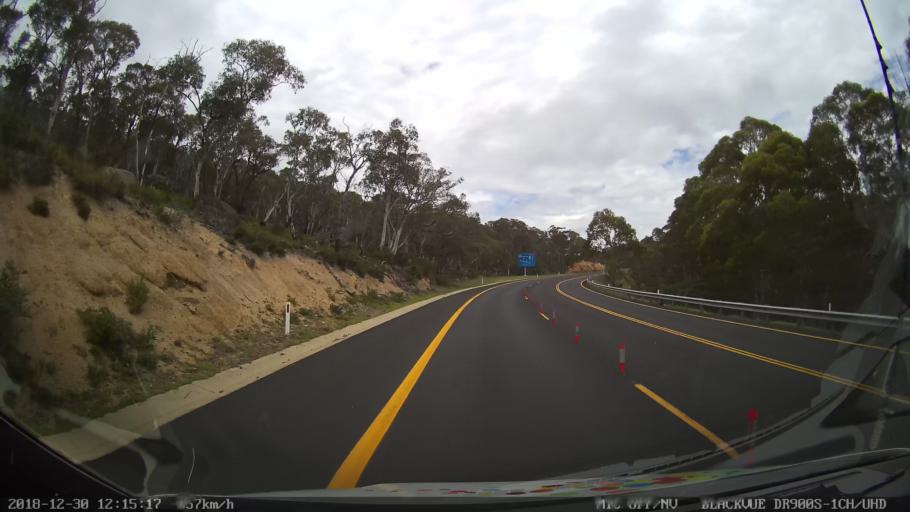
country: AU
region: New South Wales
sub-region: Snowy River
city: Jindabyne
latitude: -36.3450
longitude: 148.5729
